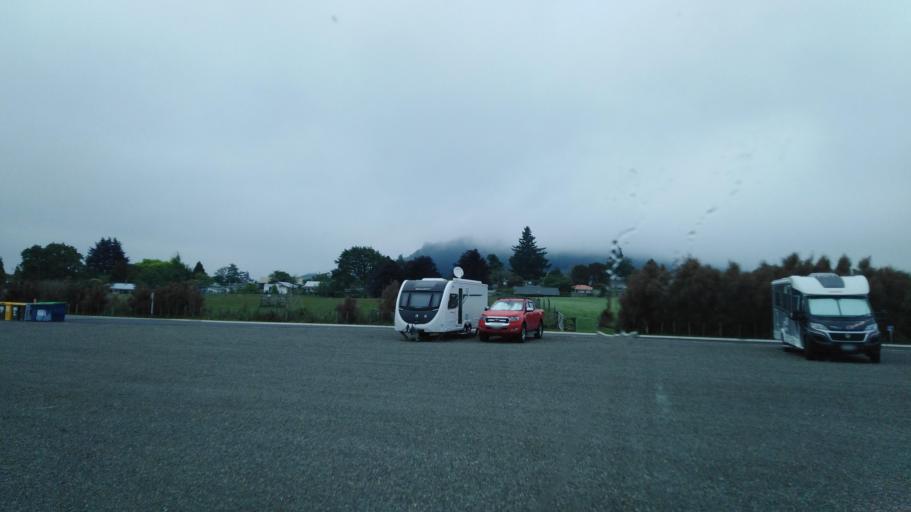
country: NZ
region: Bay of Plenty
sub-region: Rotorua District
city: Rotorua
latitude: -38.0762
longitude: 176.2080
